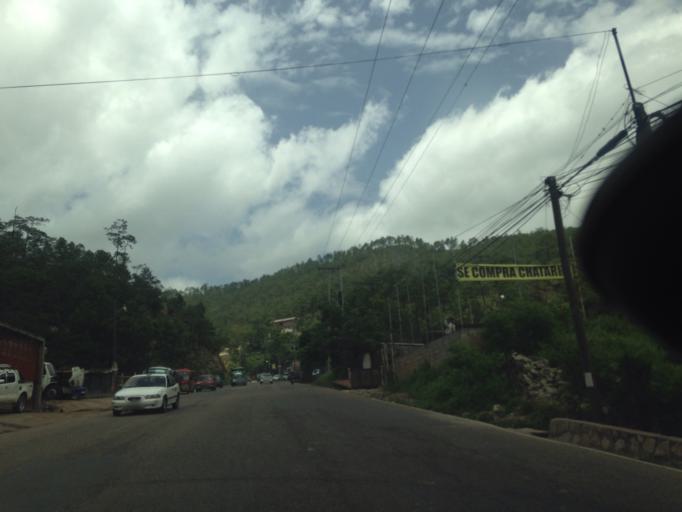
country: HN
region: Francisco Morazan
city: El Tablon
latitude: 14.0510
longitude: -87.1564
